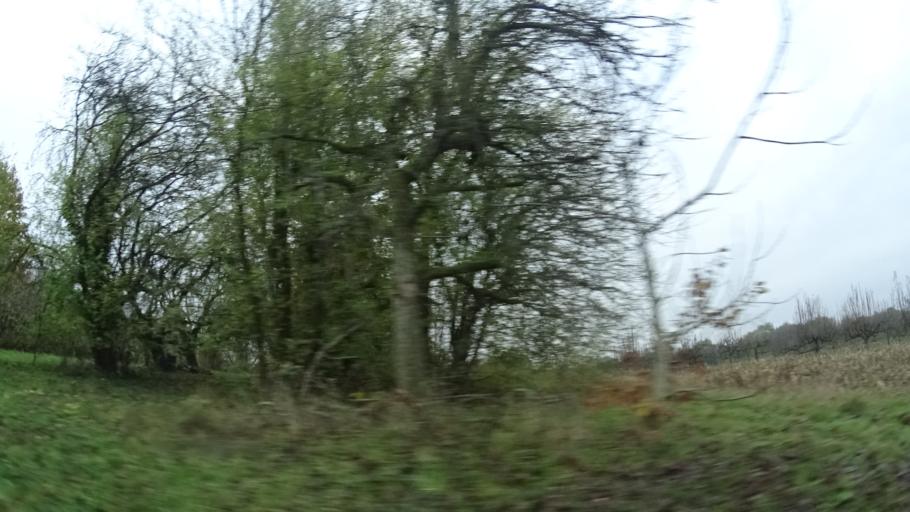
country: DE
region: Baden-Wuerttemberg
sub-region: Karlsruhe Region
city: Sinzheim
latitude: 48.7553
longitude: 8.1741
